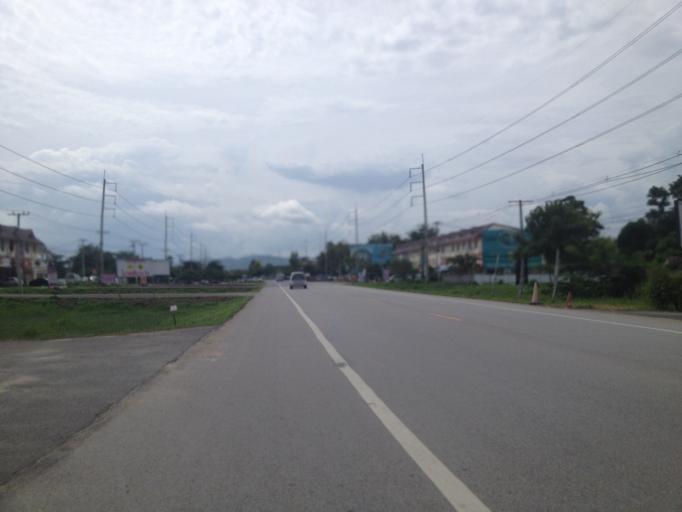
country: TH
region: Chiang Mai
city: Hang Dong
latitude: 18.7212
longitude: 98.9594
